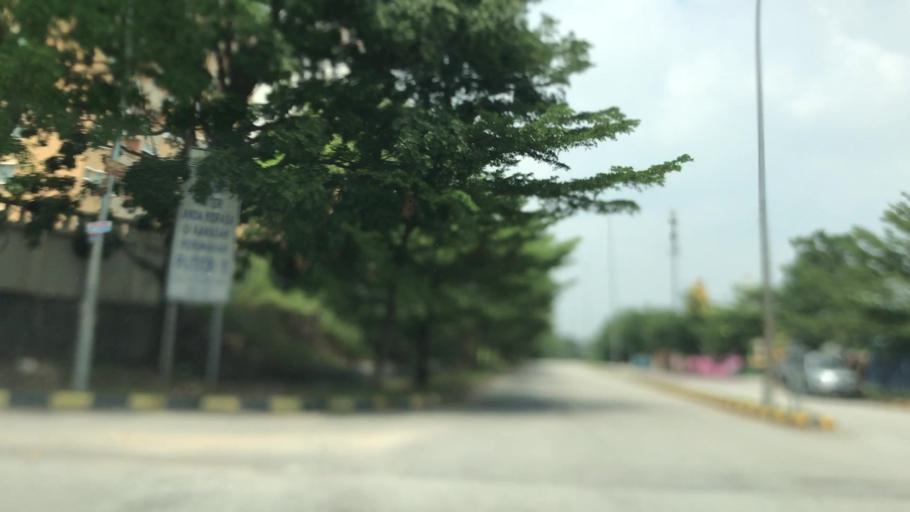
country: MY
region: Selangor
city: Subang Jaya
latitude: 3.0028
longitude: 101.6280
